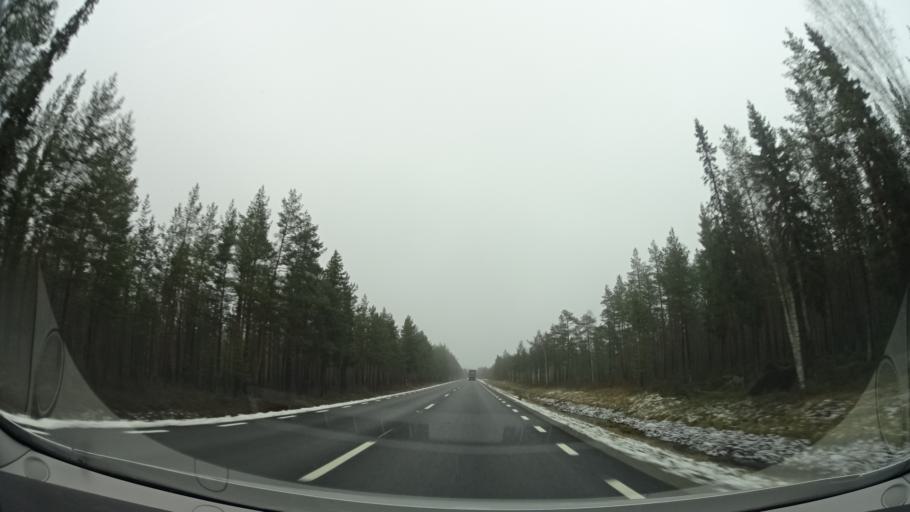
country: SE
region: Vaesterbotten
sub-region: Dorotea Kommun
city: Dorotea
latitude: 64.2518
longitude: 16.3484
